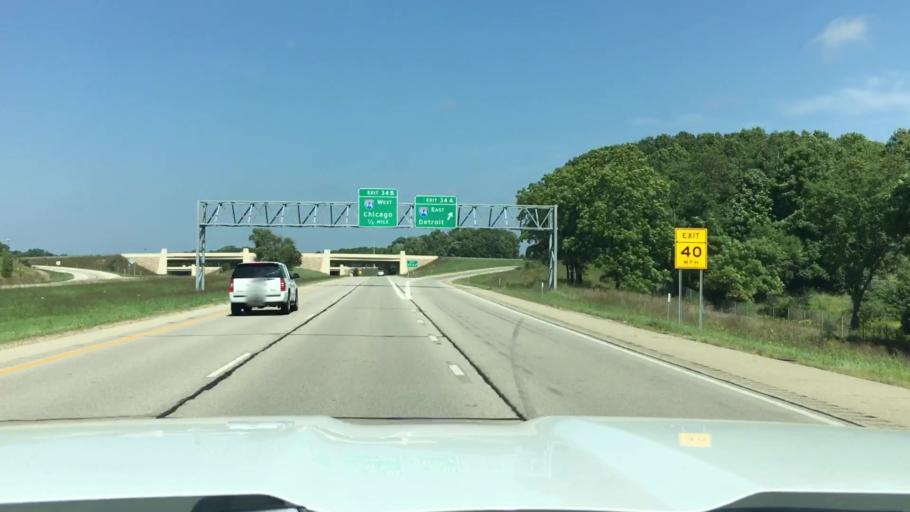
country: US
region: Michigan
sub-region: Kalamazoo County
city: Portage
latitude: 42.2324
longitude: -85.6381
